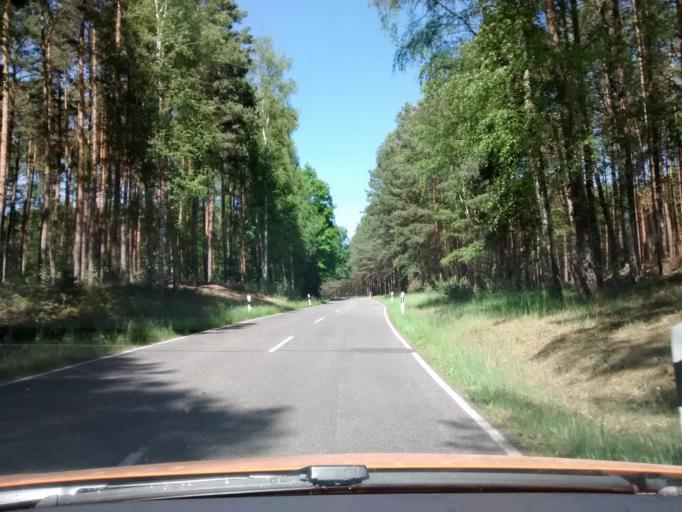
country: DE
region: Brandenburg
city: Reichenwalde
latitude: 52.2461
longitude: 13.9949
